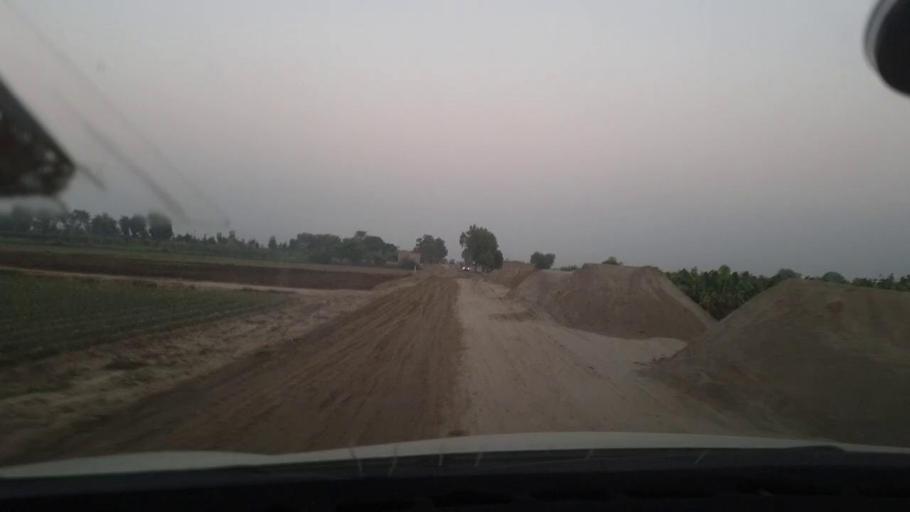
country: PK
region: Sindh
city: Tando Adam
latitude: 25.7544
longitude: 68.6136
